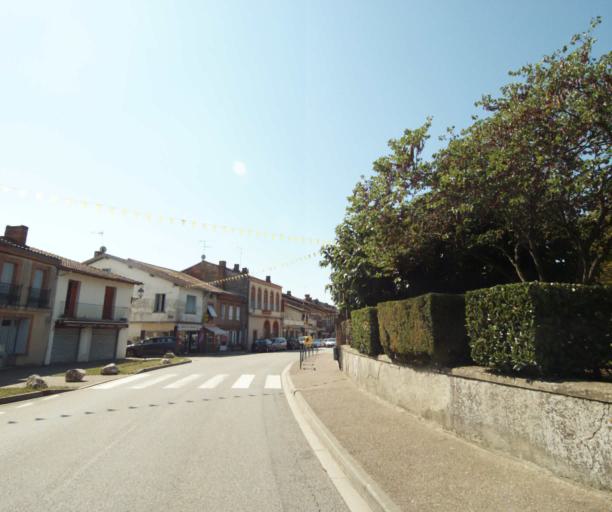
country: FR
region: Midi-Pyrenees
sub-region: Departement de l'Ariege
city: Lezat-sur-Leze
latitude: 43.2764
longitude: 1.3478
